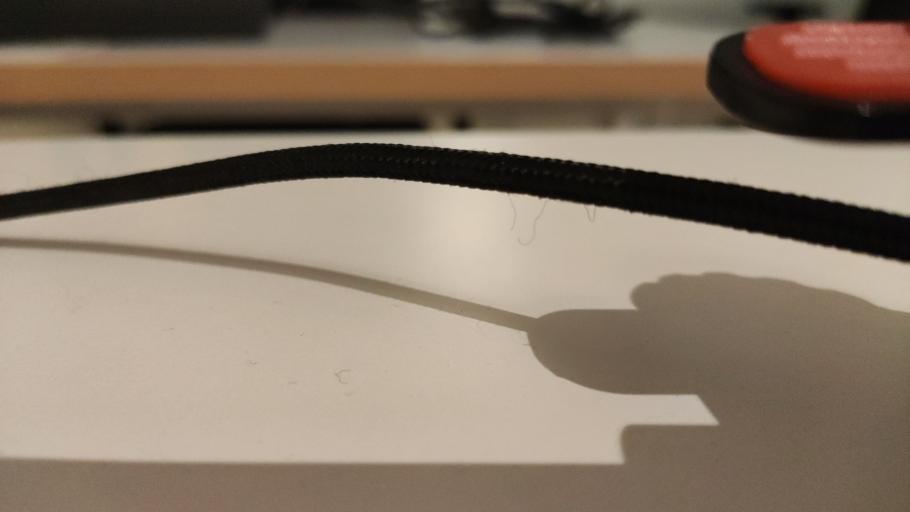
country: RU
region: Moskovskaya
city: Il'inskiy Pogost
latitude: 55.5240
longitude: 38.8720
